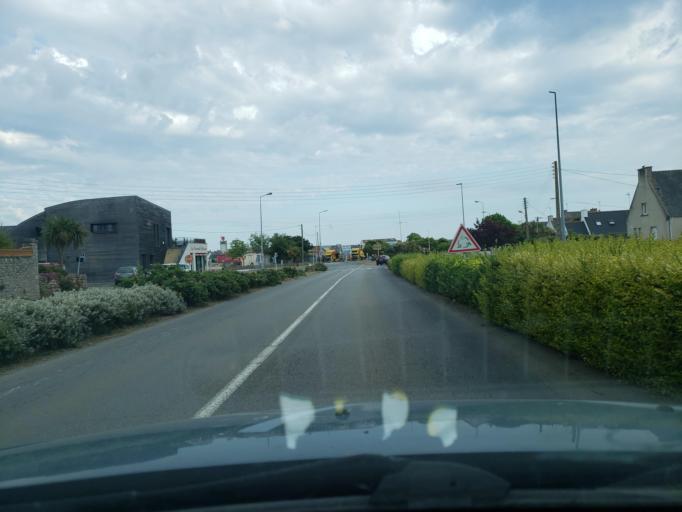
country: FR
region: Brittany
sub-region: Departement du Finistere
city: Guilvinec
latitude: 47.8007
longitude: -4.2770
